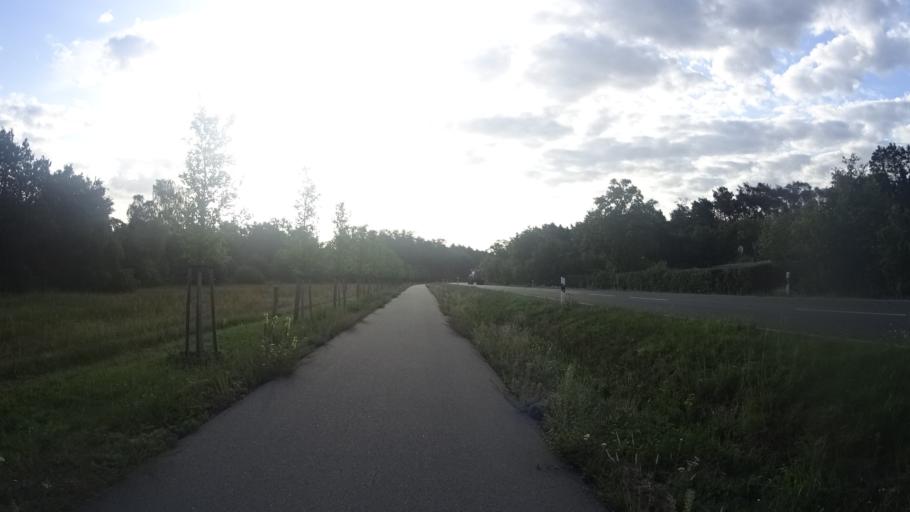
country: DE
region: Brandenburg
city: Premnitz
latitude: 52.5193
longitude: 12.3943
